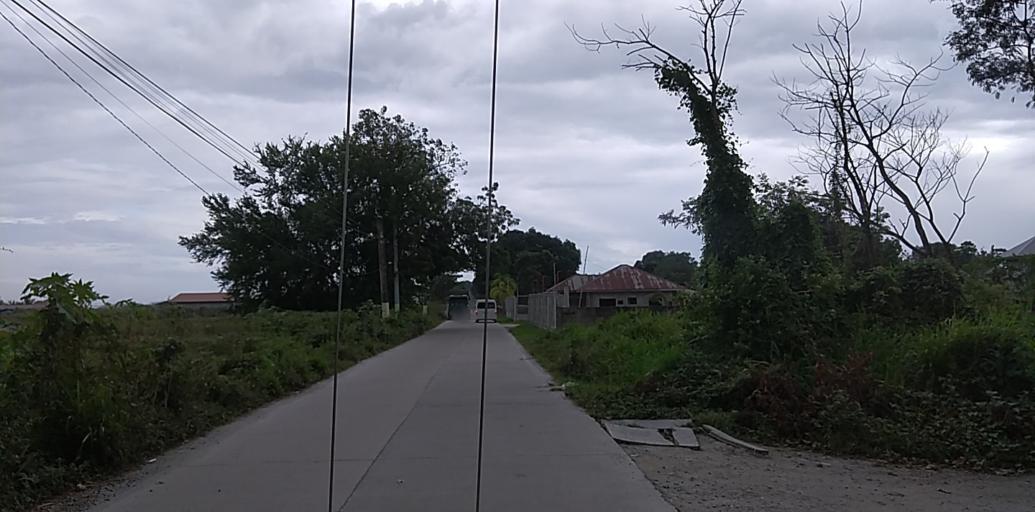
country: PH
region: Central Luzon
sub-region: Province of Pampanga
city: Porac
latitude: 15.0617
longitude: 120.5521
